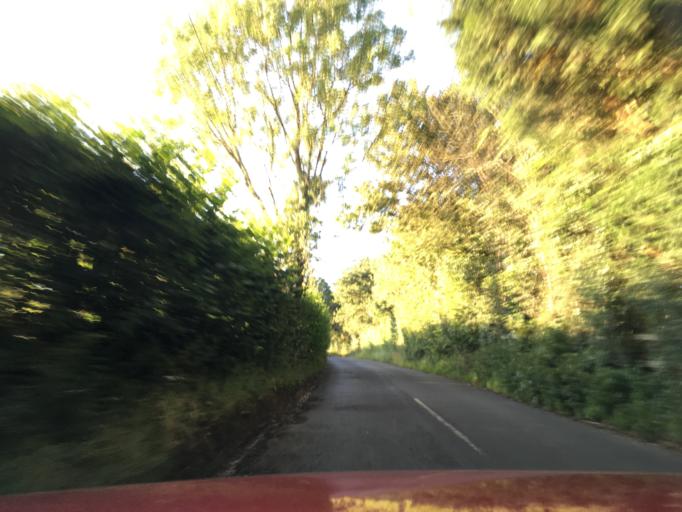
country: GB
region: England
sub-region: Hampshire
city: Tadley
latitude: 51.4213
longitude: -1.1632
